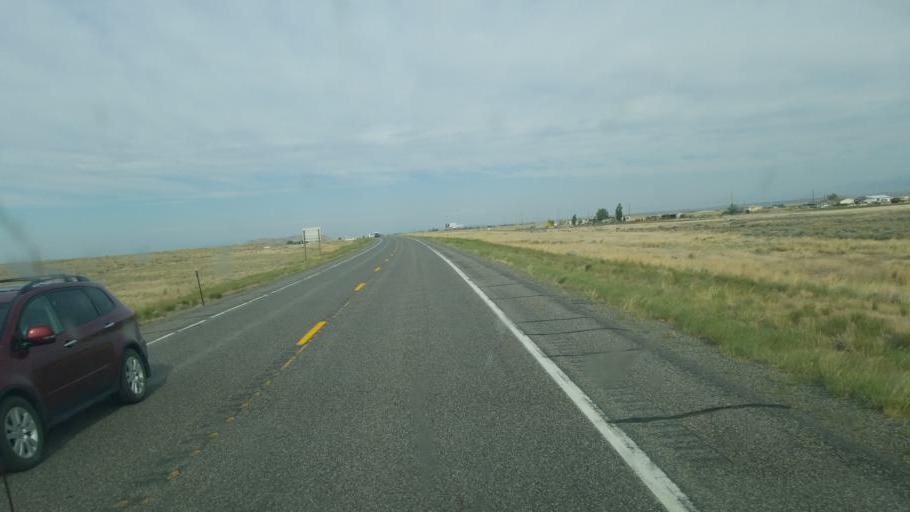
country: US
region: Wyoming
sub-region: Fremont County
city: Riverton
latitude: 43.2369
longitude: -108.0840
